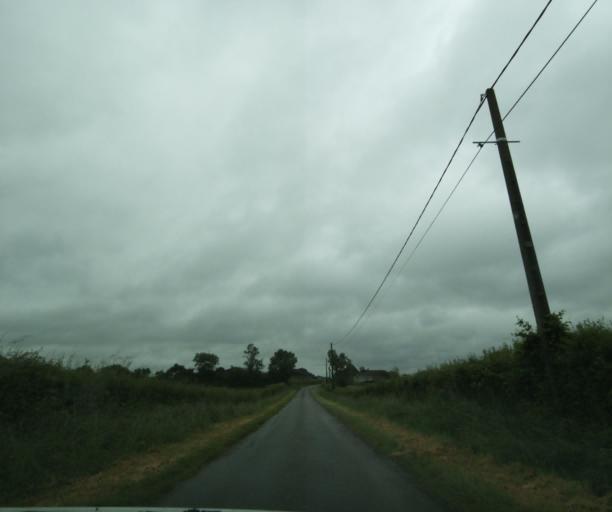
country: FR
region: Bourgogne
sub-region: Departement de Saone-et-Loire
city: Palinges
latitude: 46.5648
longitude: 4.2058
